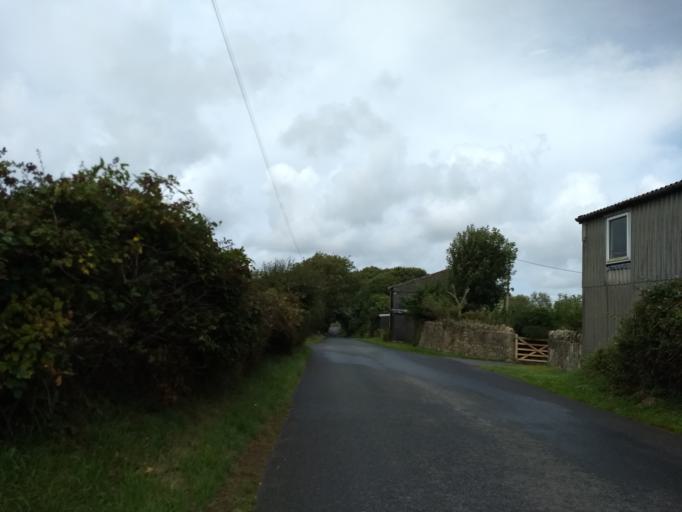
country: GB
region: England
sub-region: Isle of Wight
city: Newchurch
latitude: 50.6484
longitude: -1.2252
